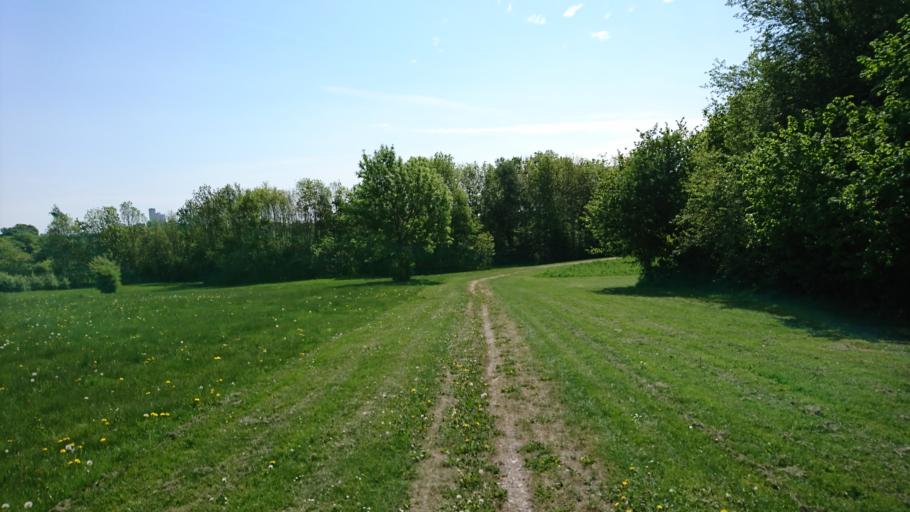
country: DK
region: Capital Region
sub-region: Ballerup Kommune
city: Ballerup
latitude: 55.7344
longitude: 12.3986
